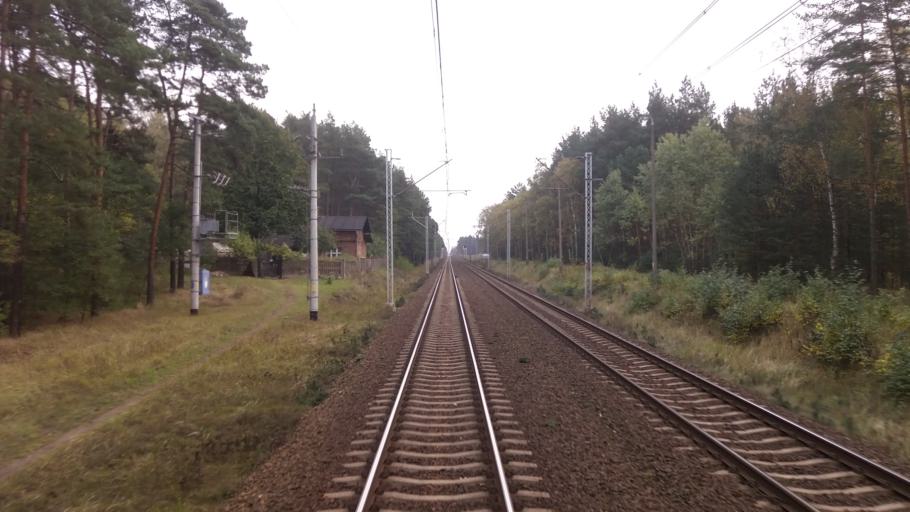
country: PL
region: West Pomeranian Voivodeship
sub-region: Powiat stargardzki
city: Kobylanka
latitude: 53.3814
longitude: 14.7802
